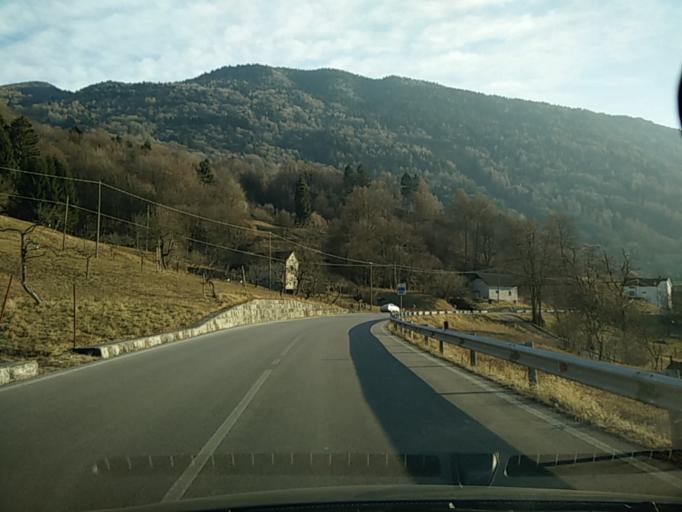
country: IT
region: Veneto
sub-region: Provincia di Belluno
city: Farra d'Alpago
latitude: 46.1112
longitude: 12.3545
